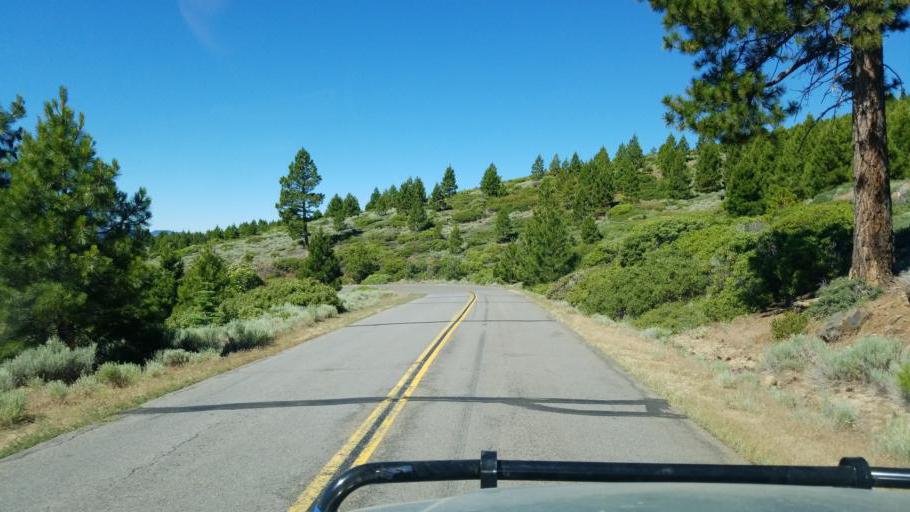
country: US
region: California
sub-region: Lassen County
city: Susanville
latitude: 40.4781
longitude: -120.7487
